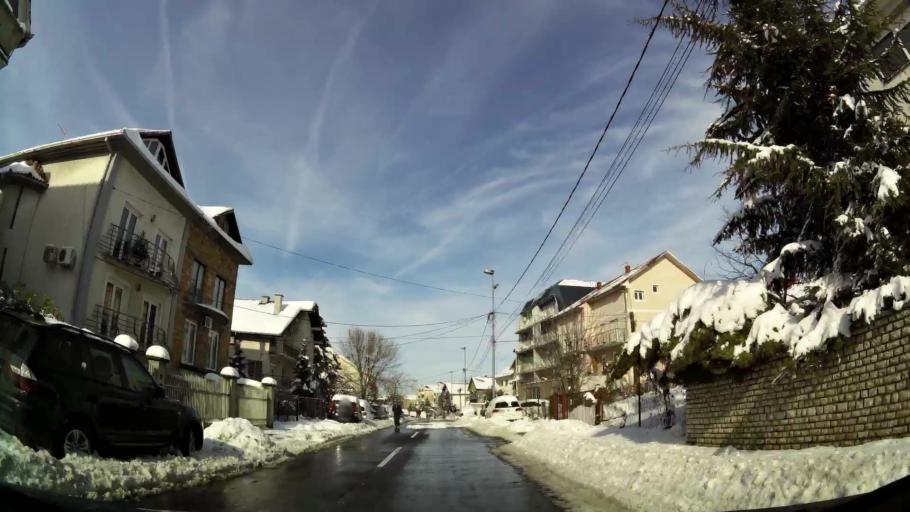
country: RS
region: Central Serbia
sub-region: Belgrade
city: Zvezdara
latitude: 44.7931
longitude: 20.5346
